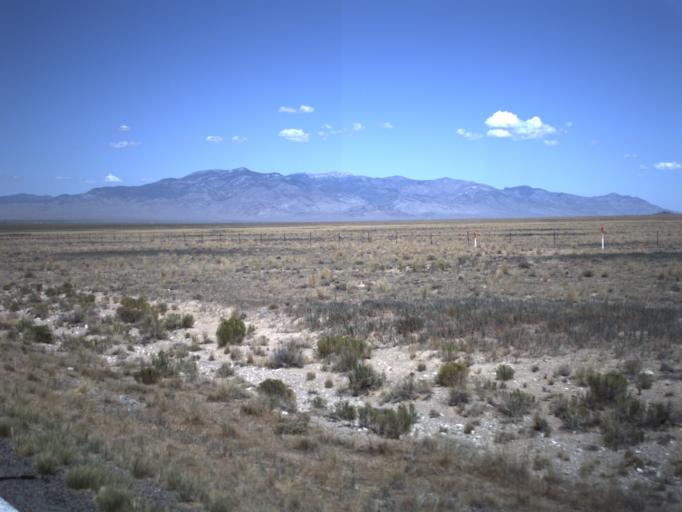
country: US
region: Nevada
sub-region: White Pine County
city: McGill
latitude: 39.0438
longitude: -113.8752
